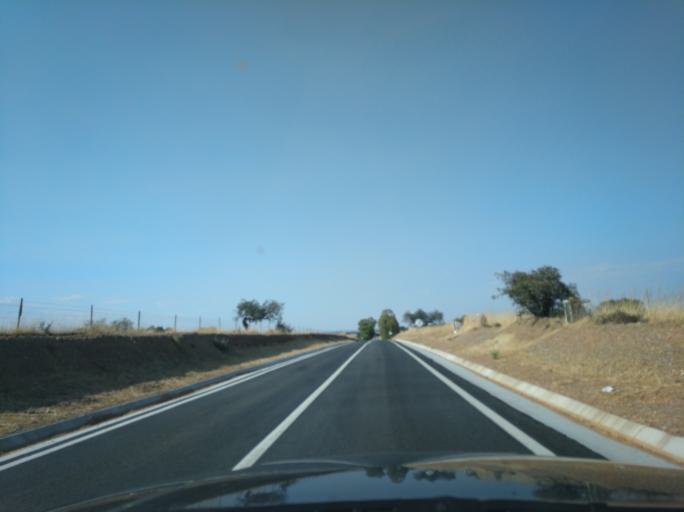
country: ES
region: Extremadura
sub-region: Provincia de Badajoz
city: Valencia del Mombuey
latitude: 38.1364
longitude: -7.2403
